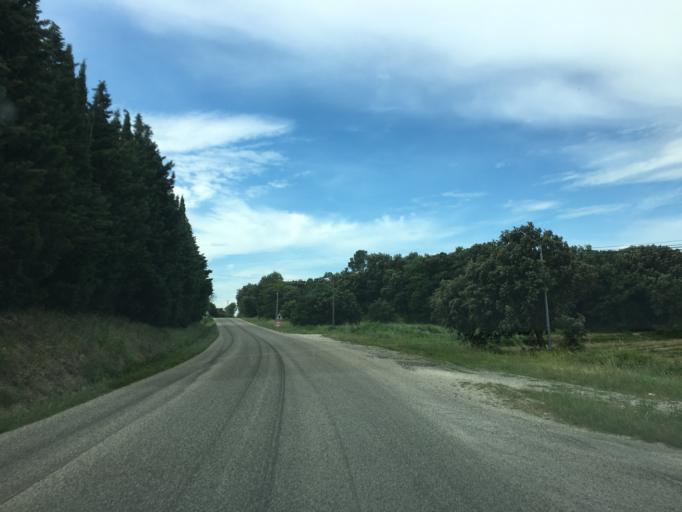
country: FR
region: Provence-Alpes-Cote d'Azur
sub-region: Departement du Vaucluse
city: Bollene
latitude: 44.2974
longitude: 4.7665
